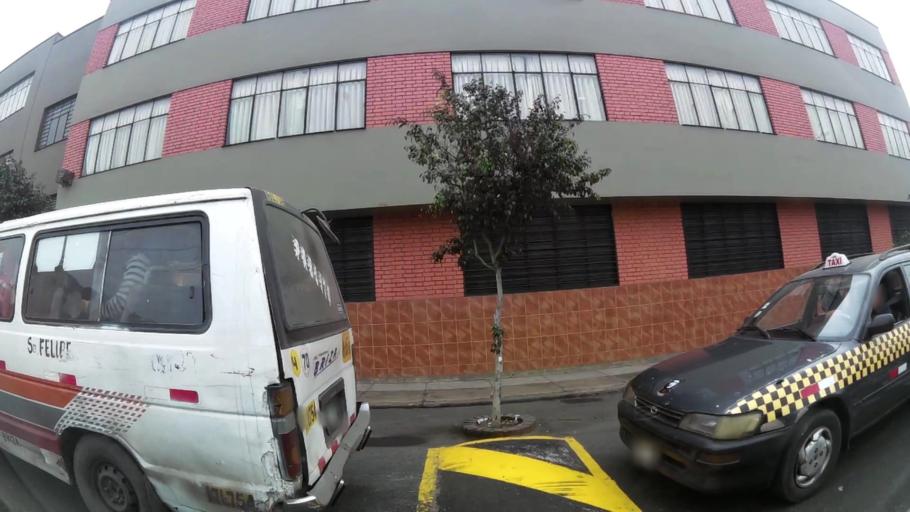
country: PE
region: Lima
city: Lima
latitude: -12.0496
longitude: -77.0508
